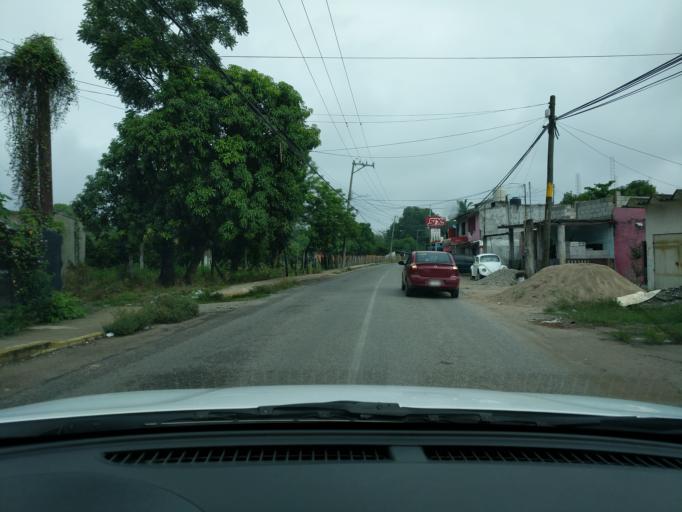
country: MX
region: Tabasco
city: Villahermosa
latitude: 17.9503
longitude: -92.9648
